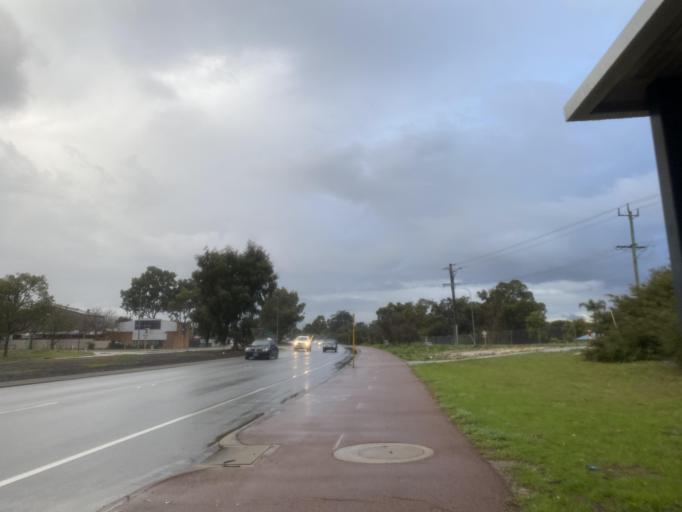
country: AU
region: Western Australia
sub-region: Canning
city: East Cannington
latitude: -32.0015
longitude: 115.9686
